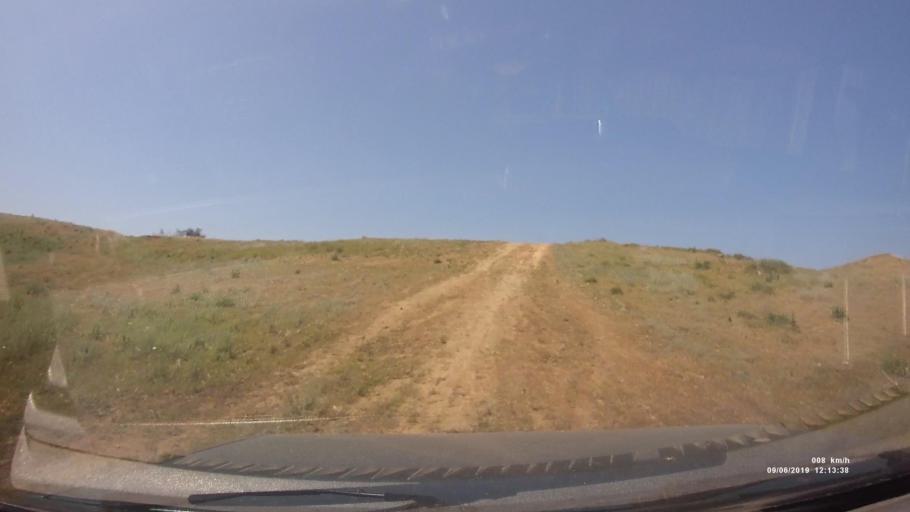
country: RU
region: Rostov
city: Staraya Stanitsa
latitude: 48.2509
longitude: 40.3270
